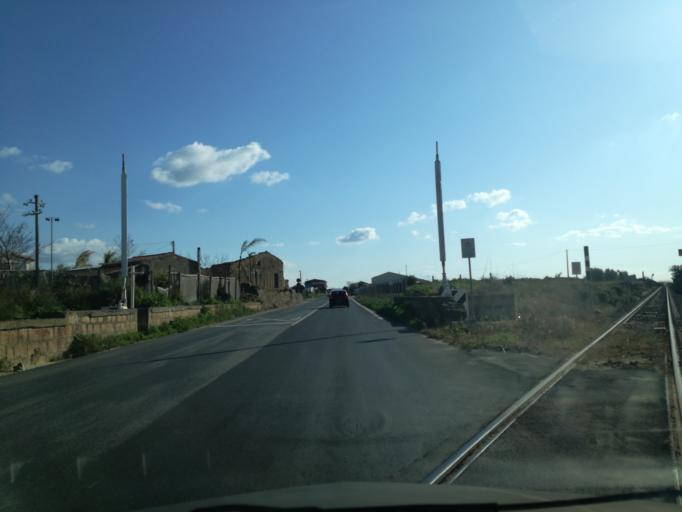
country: IT
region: Sicily
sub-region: Ragusa
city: Acate
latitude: 36.9719
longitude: 14.4747
